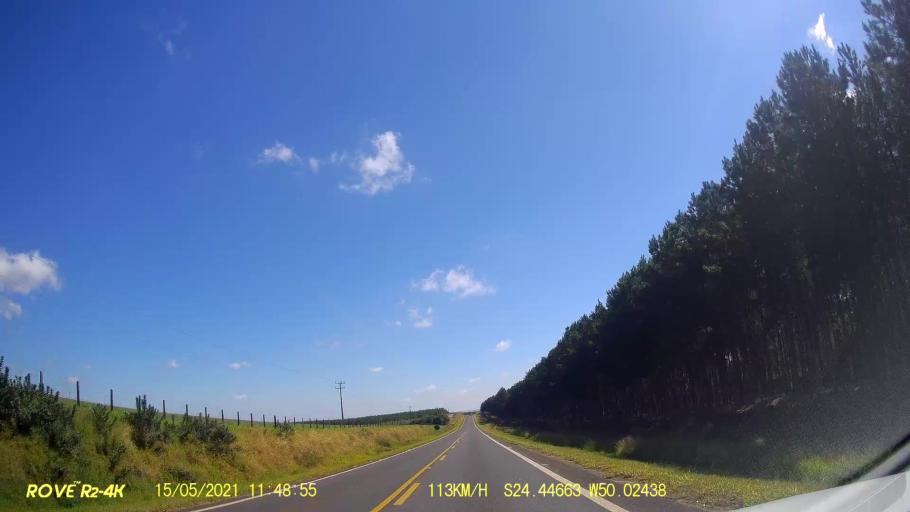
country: BR
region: Parana
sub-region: Pirai Do Sul
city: Pirai do Sul
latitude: -24.4469
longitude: -50.0242
